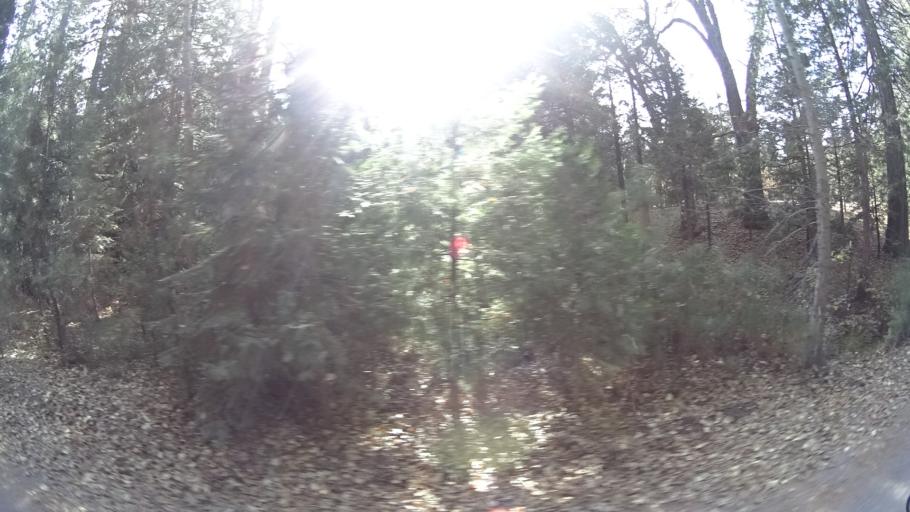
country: US
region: California
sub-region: Siskiyou County
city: Weed
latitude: 41.4345
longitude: -122.4158
